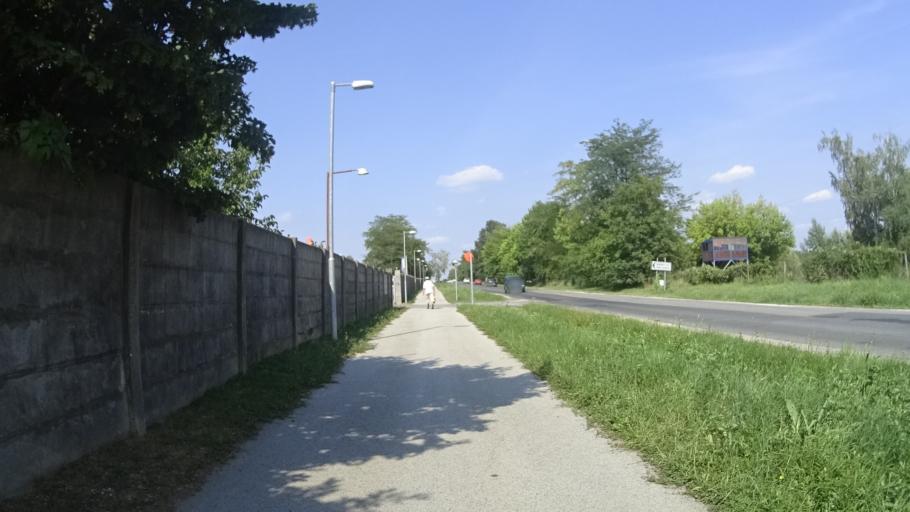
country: HU
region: Zala
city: Nagykanizsa
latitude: 46.4681
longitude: 17.0036
